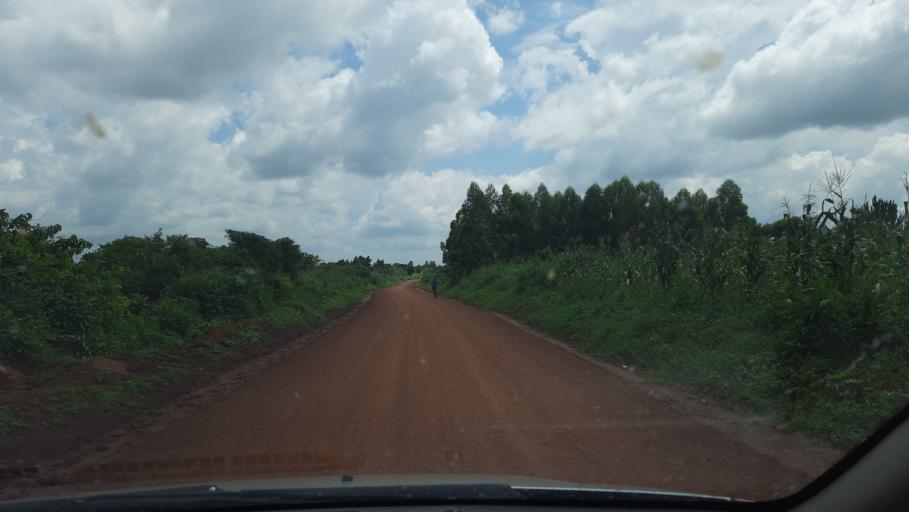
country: UG
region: Western Region
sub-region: Kiryandongo District
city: Kiryandongo
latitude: 1.8268
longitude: 31.9800
